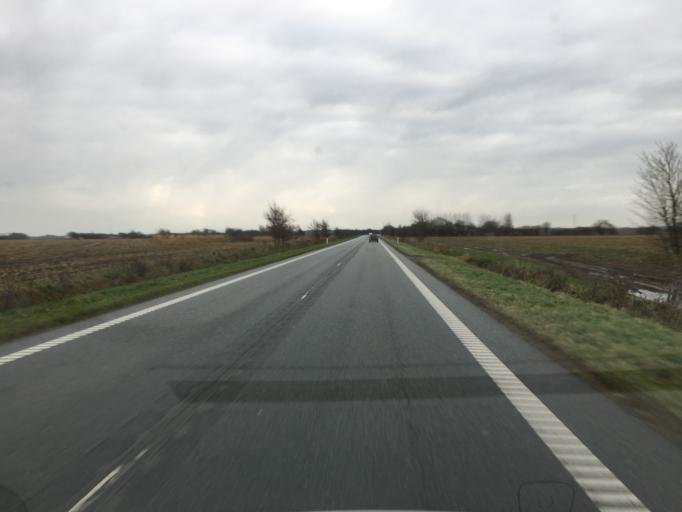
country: DK
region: South Denmark
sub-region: Tonder Kommune
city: Tonder
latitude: 55.0054
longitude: 8.8825
